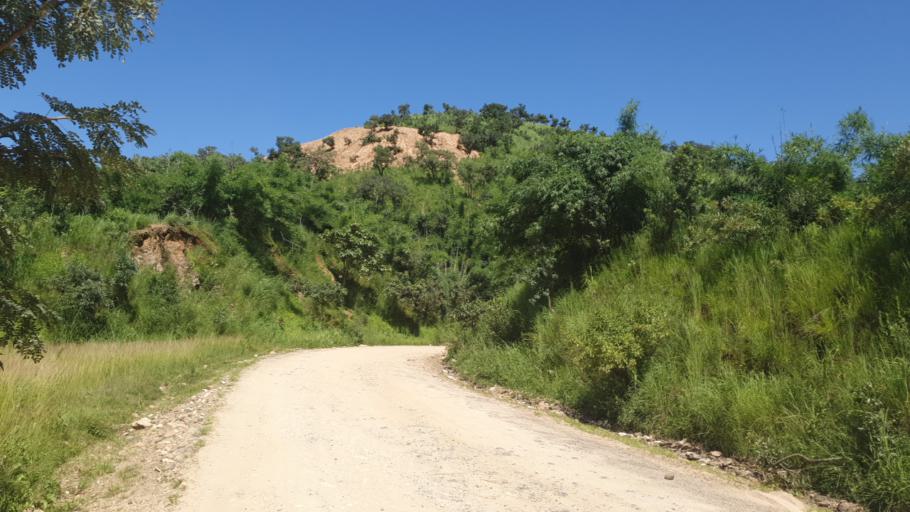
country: ET
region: Oromiya
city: Shambu
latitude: 9.7128
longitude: 36.6275
